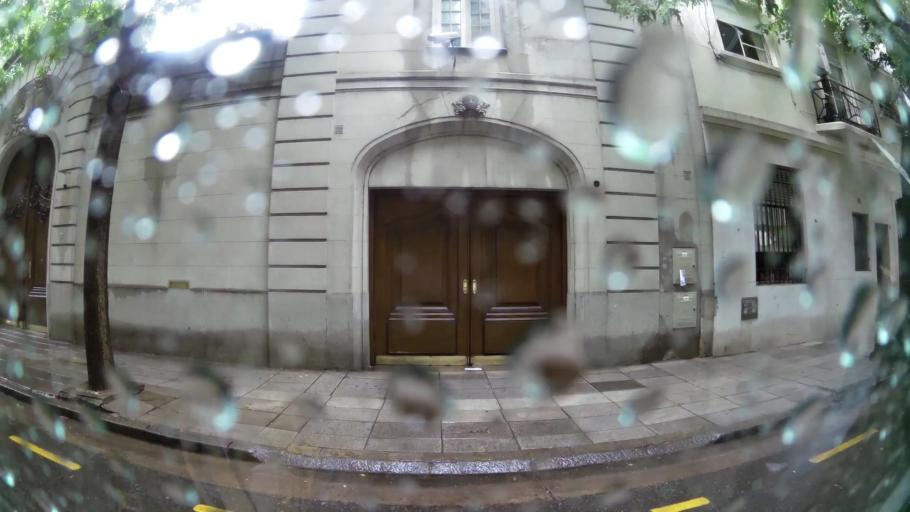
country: AR
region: Buenos Aires F.D.
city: Retiro
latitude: -34.5914
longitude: -58.3875
